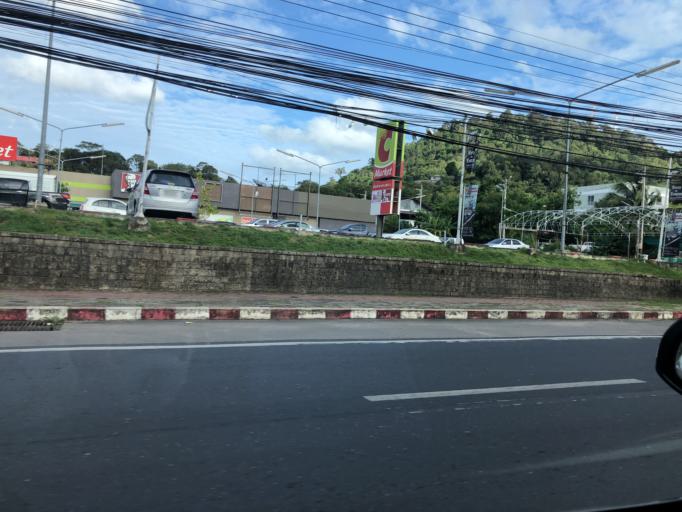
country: TH
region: Phuket
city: Ban Ratsada
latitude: 7.9093
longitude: 98.3919
